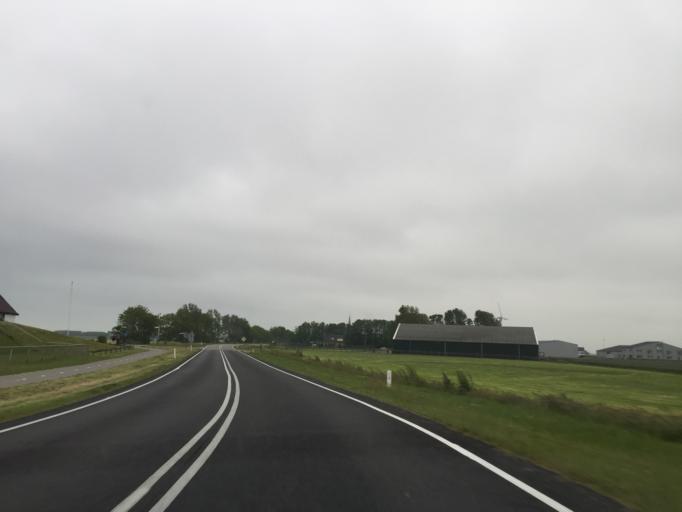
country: NL
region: Friesland
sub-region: Gemeente Dongeradeel
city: Holwerd
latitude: 53.3783
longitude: 5.8885
